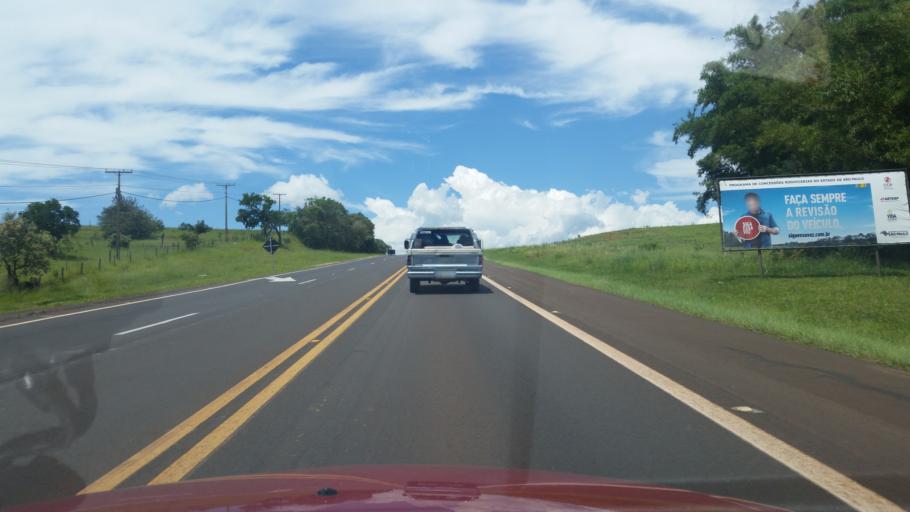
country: BR
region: Sao Paulo
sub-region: Itai
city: Itai
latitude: -23.2850
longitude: -49.0303
